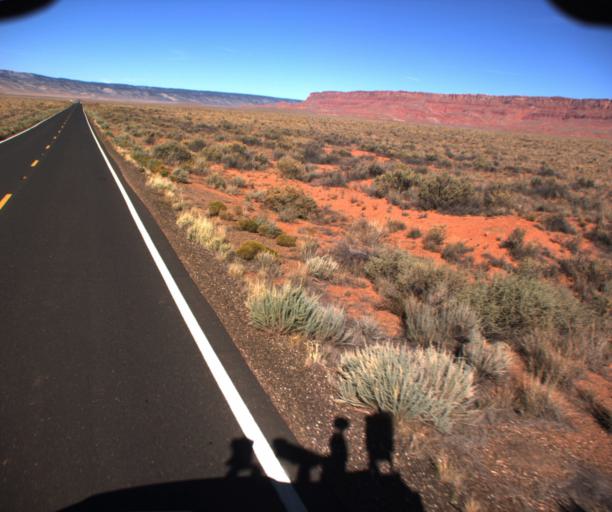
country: US
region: Arizona
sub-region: Coconino County
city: Page
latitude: 36.6945
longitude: -111.9021
